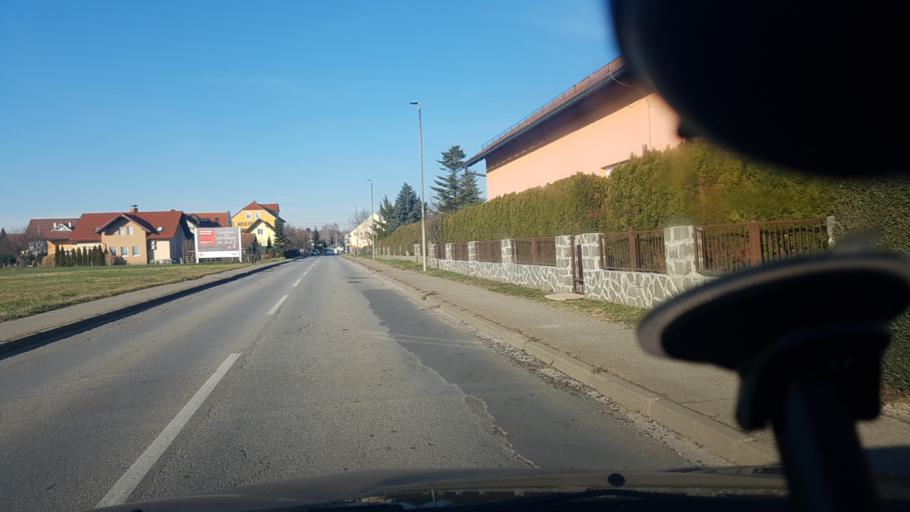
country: SI
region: Ptuj
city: Ptuj
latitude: 46.4125
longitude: 15.8649
